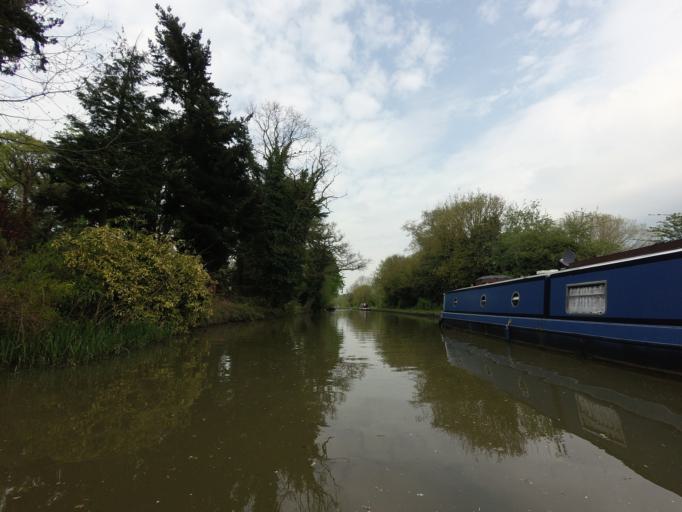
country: GB
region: England
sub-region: Central Bedfordshire
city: Leighton Buzzard
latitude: 51.9250
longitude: -0.6661
